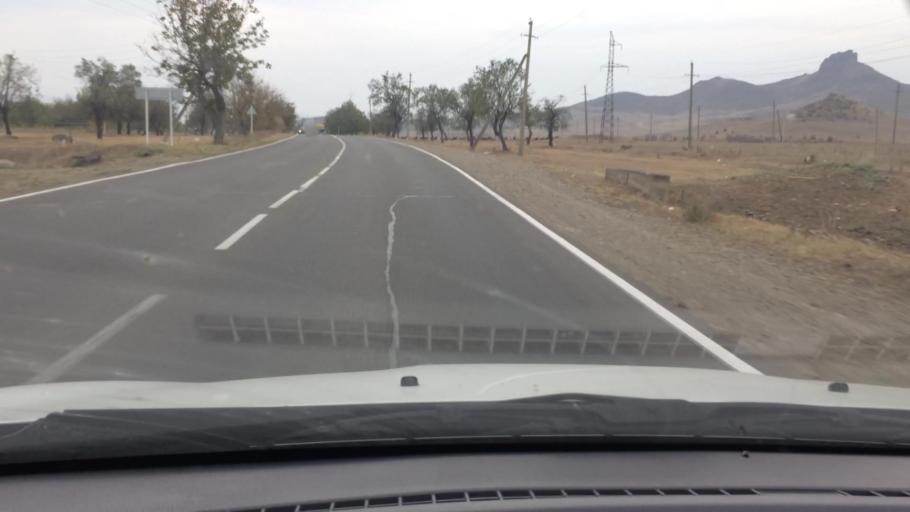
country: GE
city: Naghvarevi
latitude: 41.3861
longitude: 44.8293
